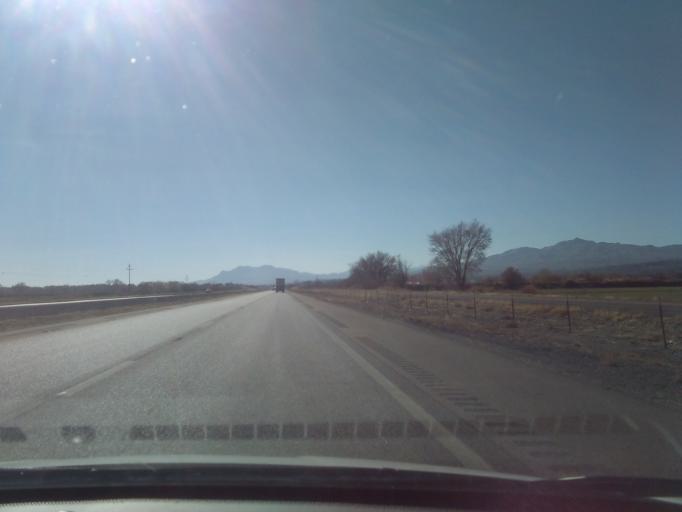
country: US
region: New Mexico
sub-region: Socorro County
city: Socorro
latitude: 34.2651
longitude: -106.9047
